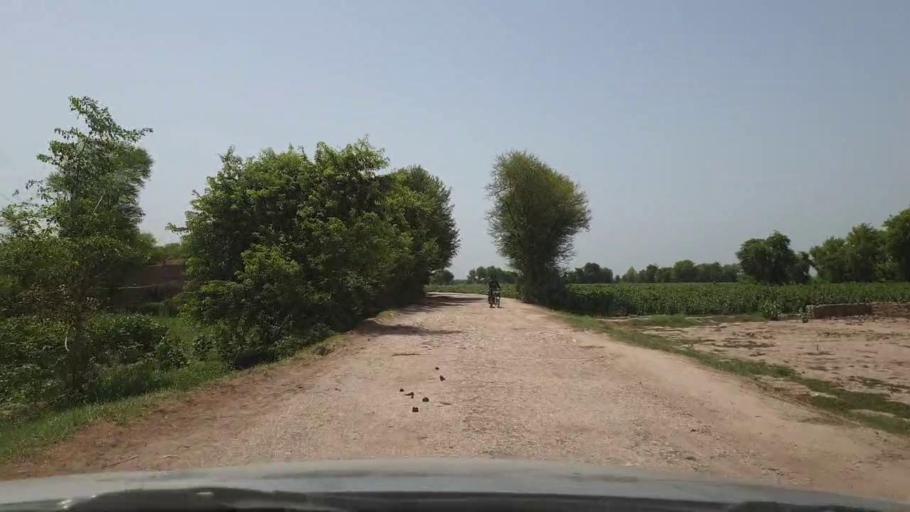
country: PK
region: Sindh
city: Pano Aqil
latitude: 27.7944
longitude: 69.2406
